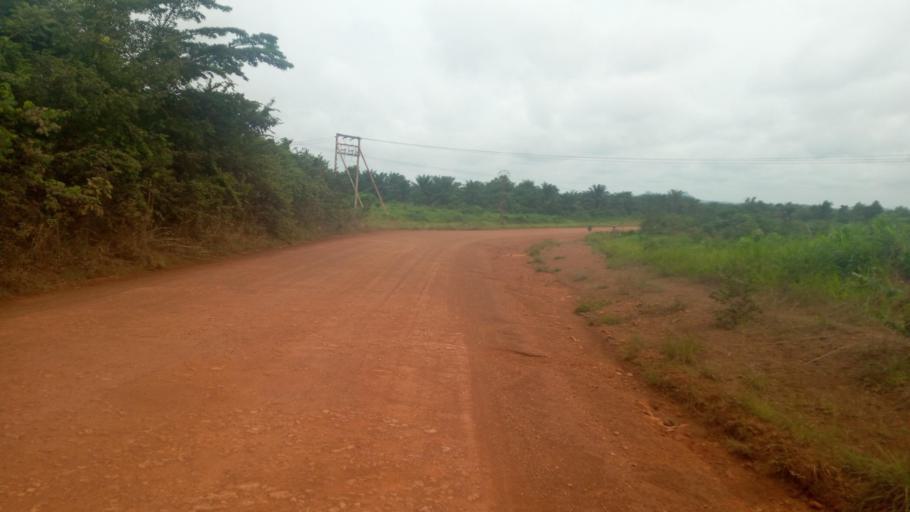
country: SL
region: Southern Province
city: Mogbwemo
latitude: 7.7410
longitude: -12.2882
